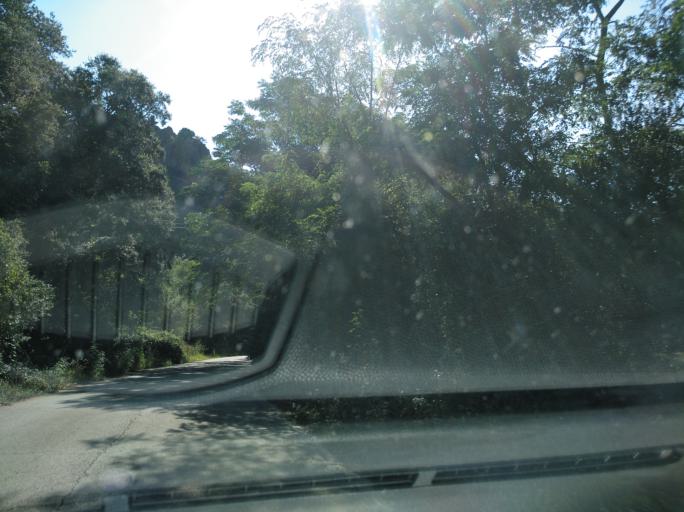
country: ES
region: Catalonia
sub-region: Provincia de Girona
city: la Cellera de Ter
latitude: 41.9830
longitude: 2.5859
